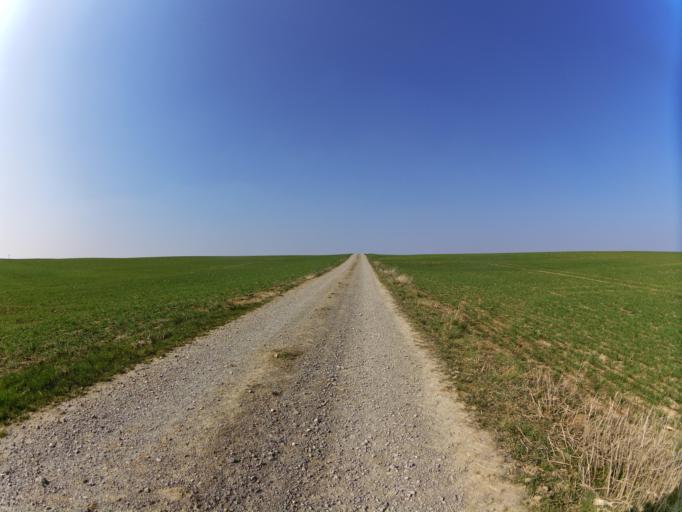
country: DE
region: Bavaria
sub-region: Regierungsbezirk Unterfranken
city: Gaukonigshofen
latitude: 49.6670
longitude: 9.9874
